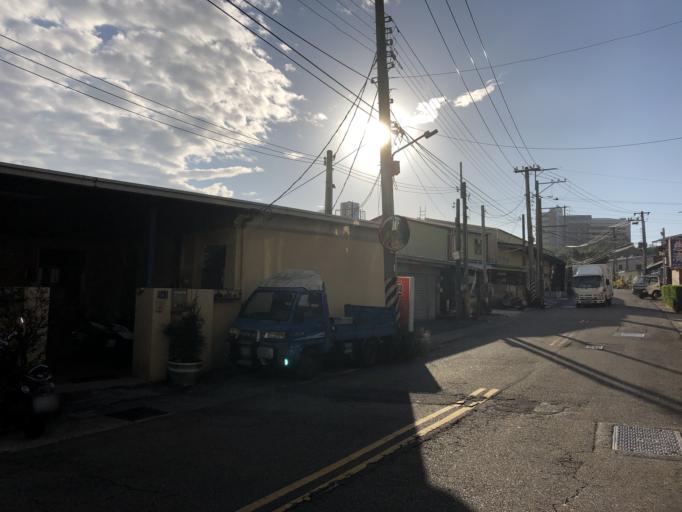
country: TW
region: Taiwan
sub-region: Changhua
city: Chang-hua
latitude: 24.1363
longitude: 120.6047
